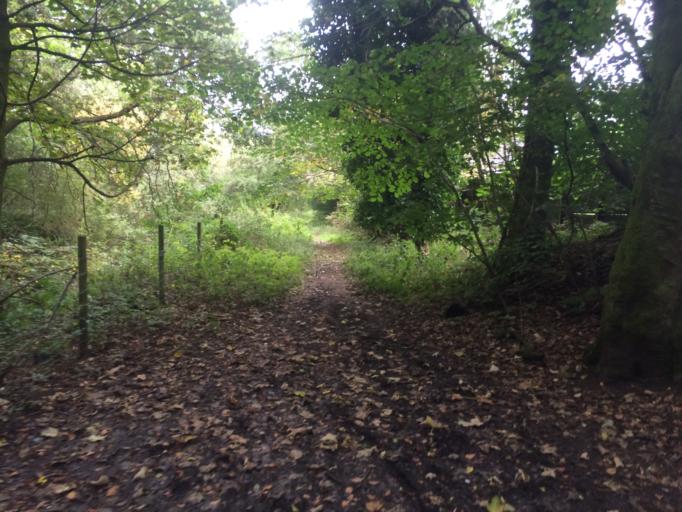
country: GB
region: Scotland
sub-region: East Dunbartonshire
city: Bishopbriggs
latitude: 55.9158
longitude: -4.2397
